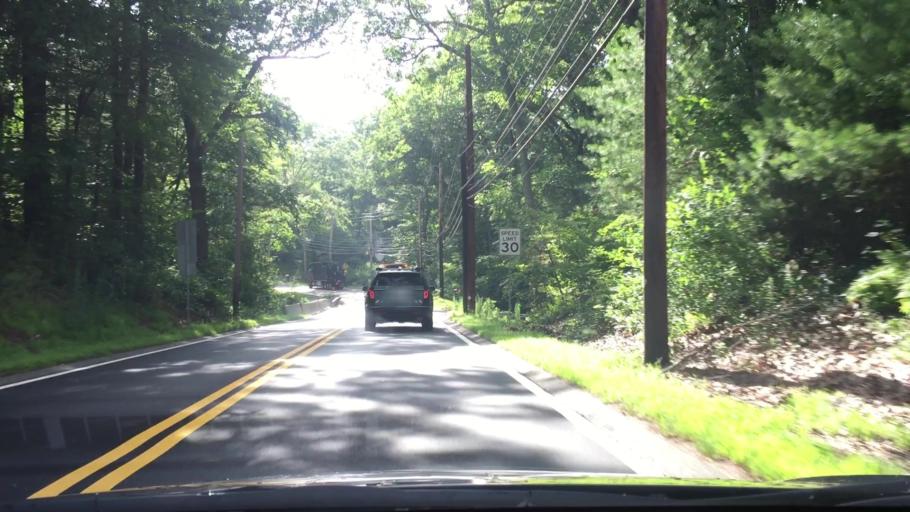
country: US
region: Massachusetts
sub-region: Middlesex County
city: Stow
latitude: 42.4808
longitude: -71.5026
